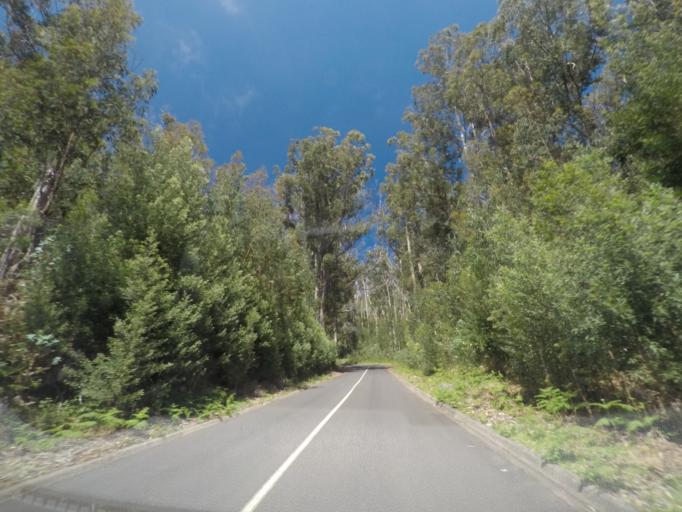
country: PT
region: Madeira
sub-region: Calheta
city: Arco da Calheta
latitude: 32.7364
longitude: -17.1324
